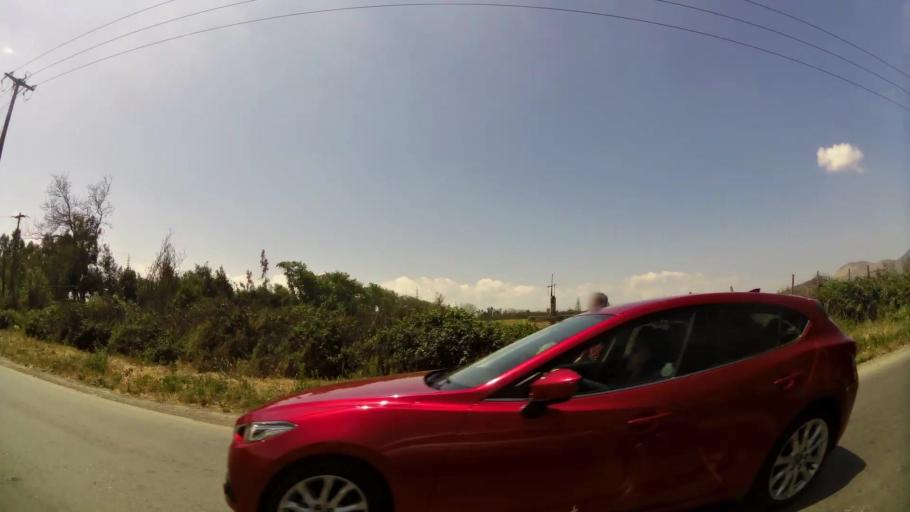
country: CL
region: Santiago Metropolitan
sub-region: Provincia de Maipo
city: San Bernardo
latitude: -33.5343
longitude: -70.7349
